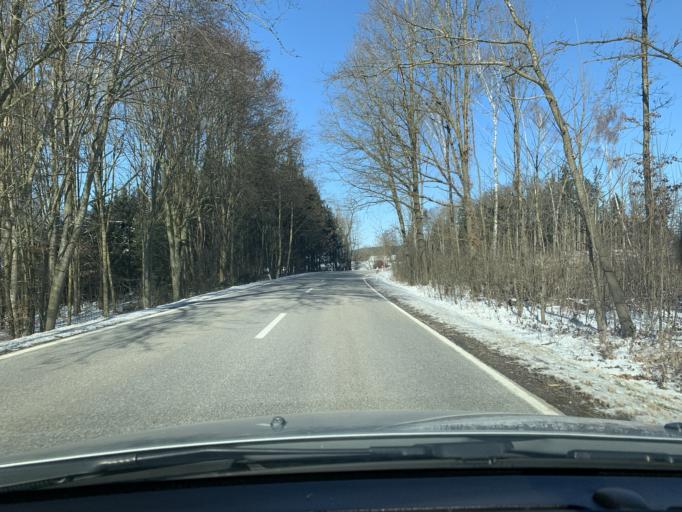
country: DE
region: Bavaria
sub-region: Upper Bavaria
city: Zangberg
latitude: 48.2977
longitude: 12.4325
